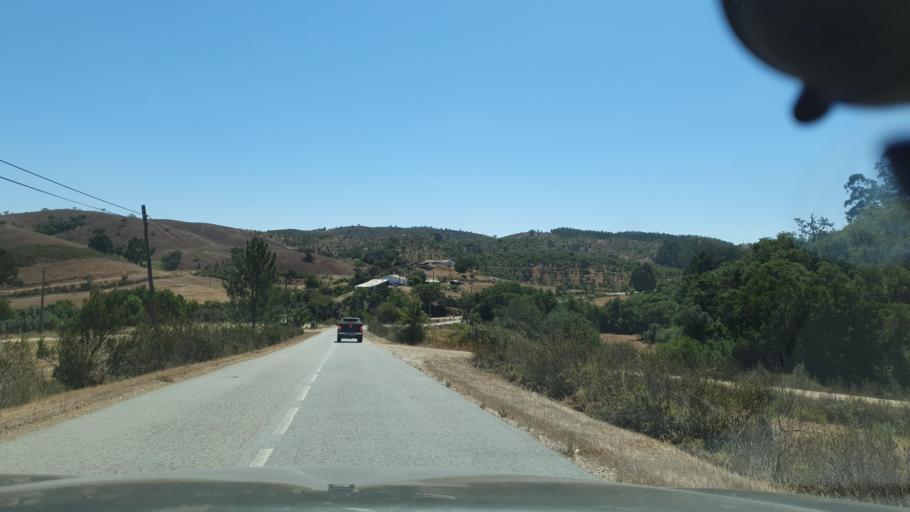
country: PT
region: Faro
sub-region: Monchique
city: Monchique
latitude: 37.4339
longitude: -8.5623
